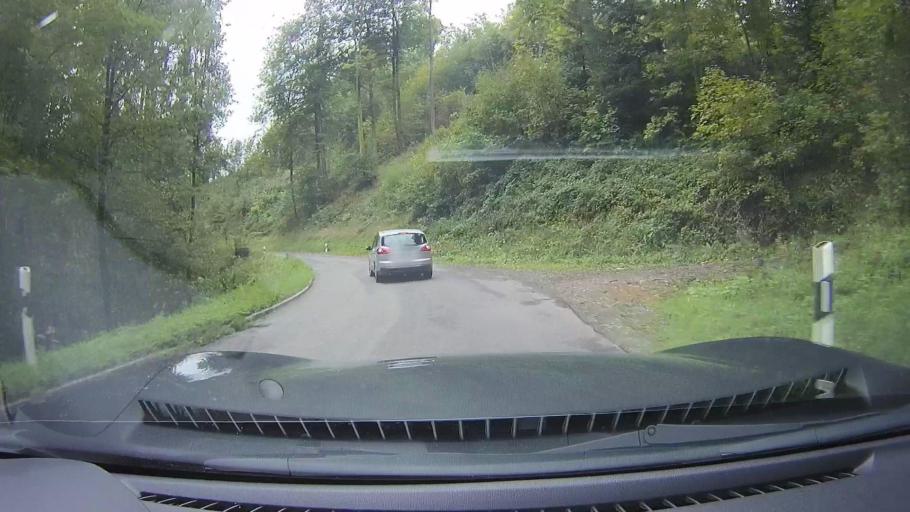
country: DE
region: Baden-Wuerttemberg
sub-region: Regierungsbezirk Stuttgart
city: Murrhardt
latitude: 48.9945
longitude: 9.5717
